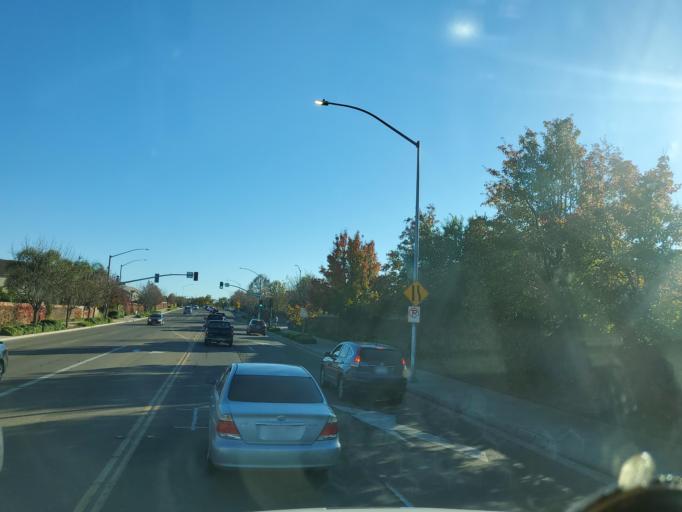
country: US
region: California
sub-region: San Joaquin County
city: August
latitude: 38.0025
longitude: -121.2714
